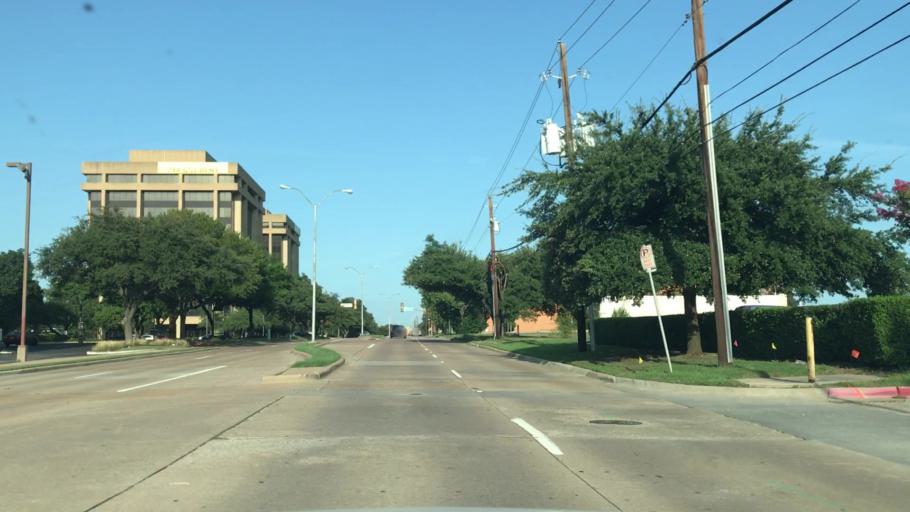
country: US
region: Texas
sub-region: Dallas County
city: Addison
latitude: 32.9328
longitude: -96.8091
